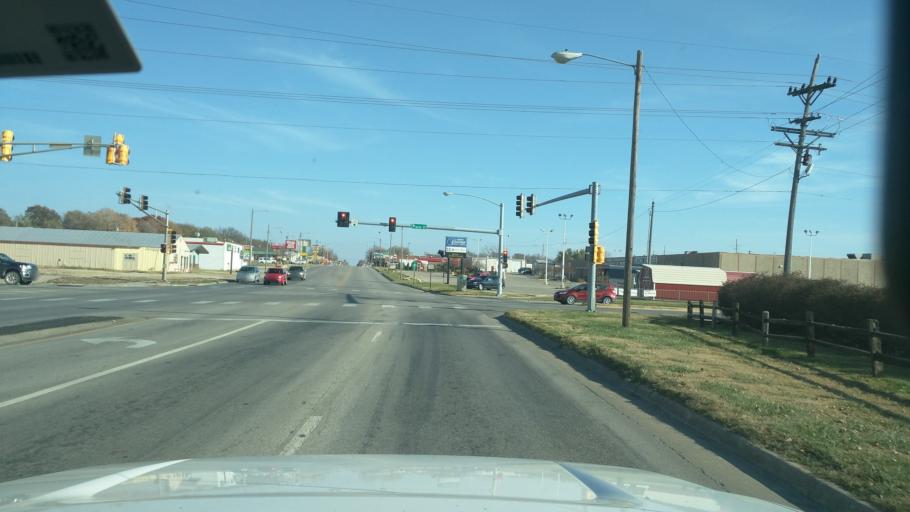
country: US
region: Kansas
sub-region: Lyon County
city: Emporia
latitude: 38.4050
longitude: -96.2086
